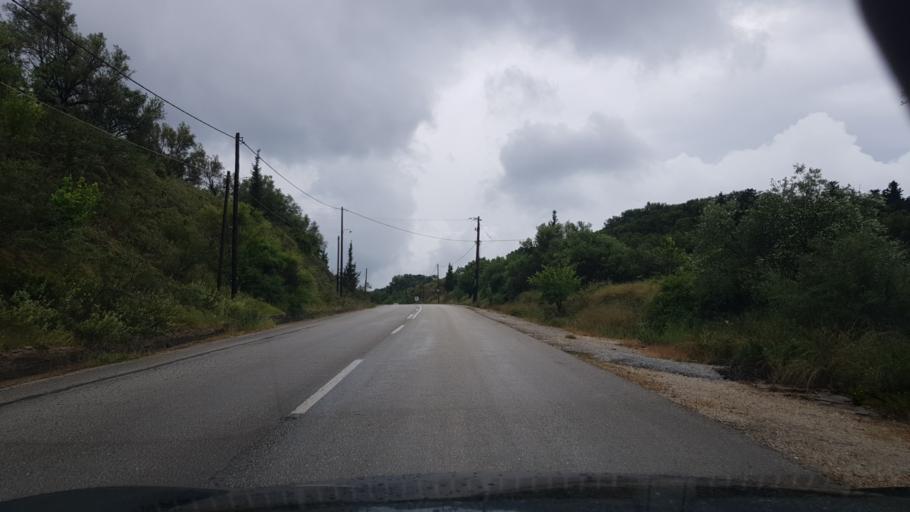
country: GR
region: Ionian Islands
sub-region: Lefkada
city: Nidri
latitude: 38.6333
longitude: 20.6280
